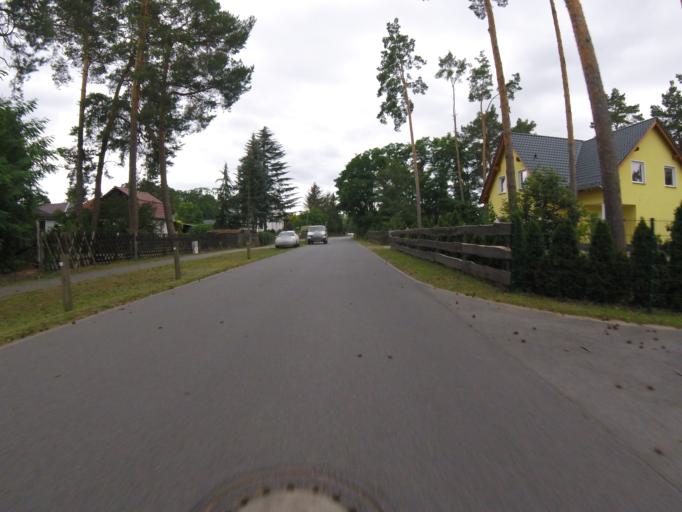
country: DE
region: Brandenburg
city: Bestensee
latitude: 52.2270
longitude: 13.6369
